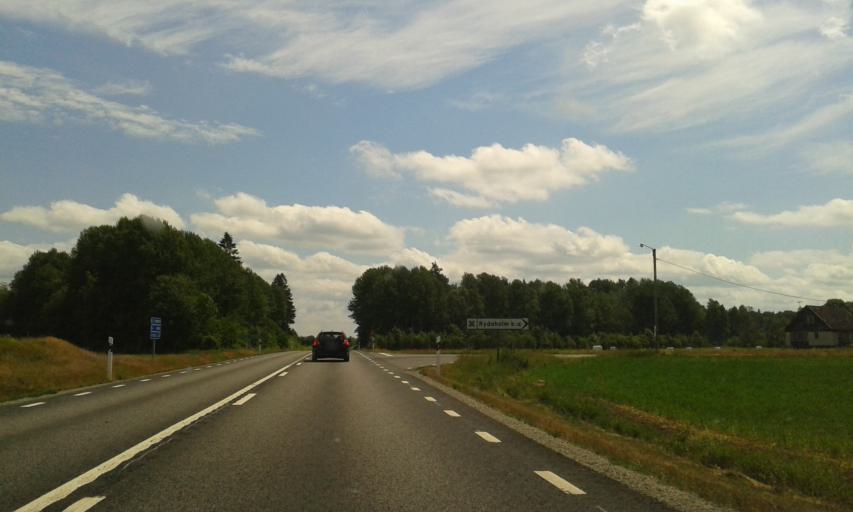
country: SE
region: Joenkoeping
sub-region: Varnamo Kommun
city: Rydaholm
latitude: 57.0016
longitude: 14.2734
